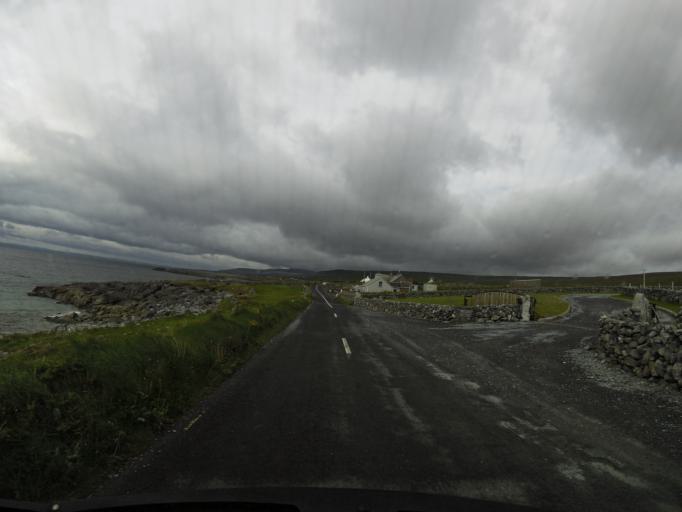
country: IE
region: Connaught
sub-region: County Galway
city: Bearna
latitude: 53.0885
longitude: -9.3150
